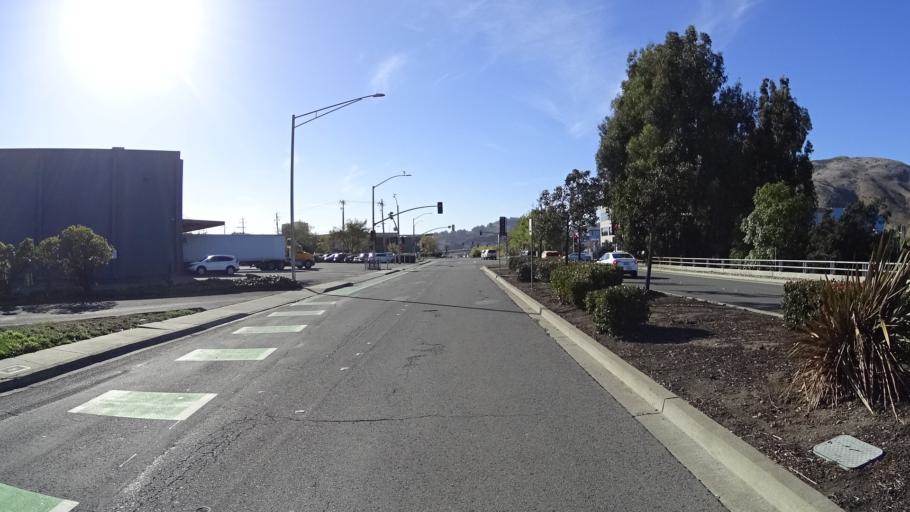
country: US
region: California
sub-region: San Mateo County
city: South San Francisco
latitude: 37.6625
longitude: -122.3873
